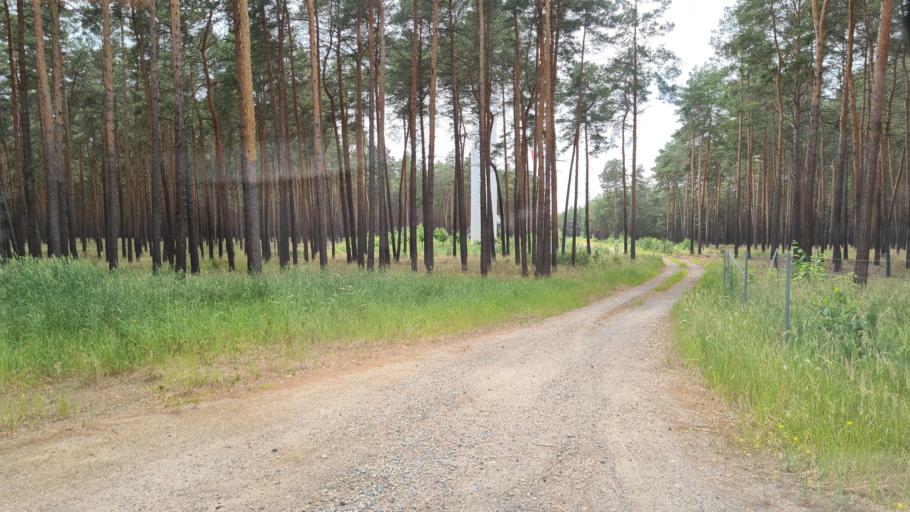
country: DE
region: Brandenburg
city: Schilda
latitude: 51.6606
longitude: 13.3516
